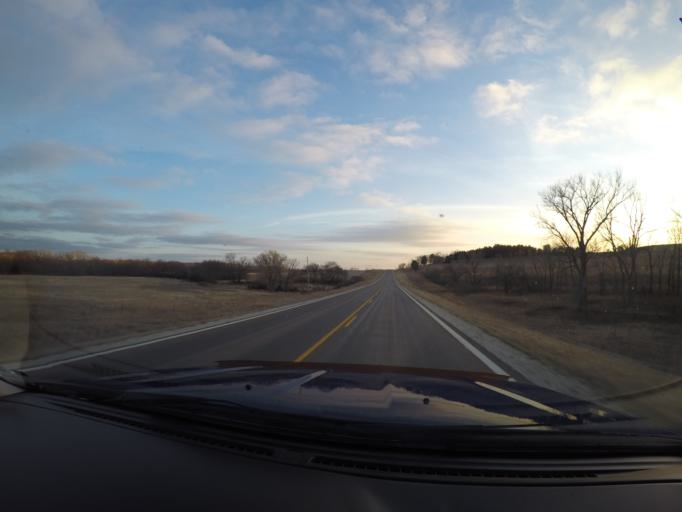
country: US
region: Kansas
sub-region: Chase County
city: Cottonwood Falls
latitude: 38.4382
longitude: -96.5570
